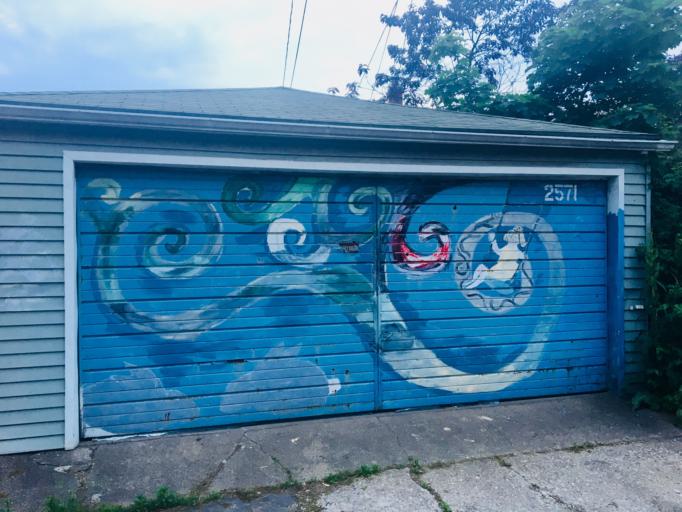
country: US
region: Michigan
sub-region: Wayne County
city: River Rouge
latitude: 42.3157
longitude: -83.1256
